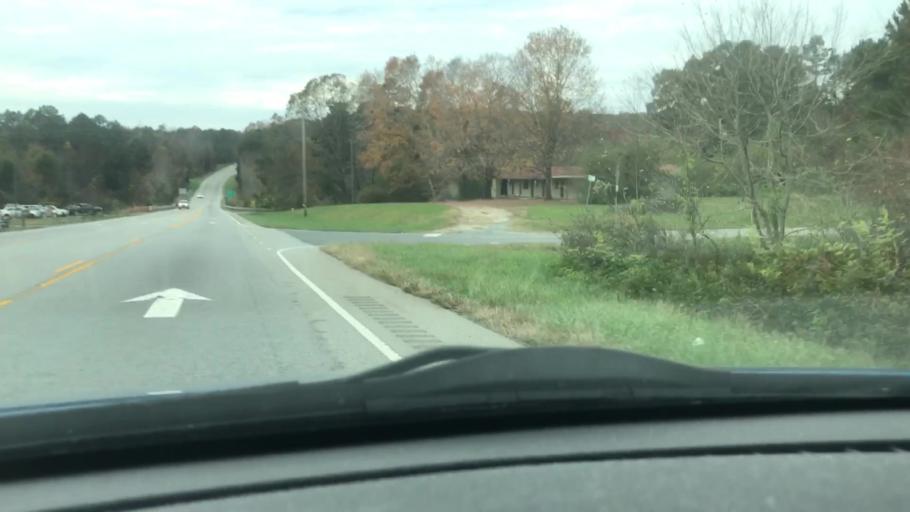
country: US
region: North Carolina
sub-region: Randolph County
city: Trinity
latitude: 35.7355
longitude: -79.9792
